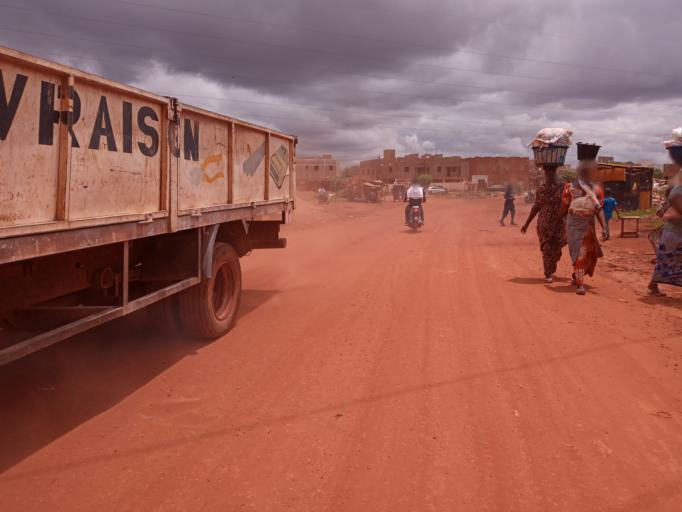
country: ML
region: Bamako
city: Bamako
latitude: 12.5475
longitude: -7.9953
